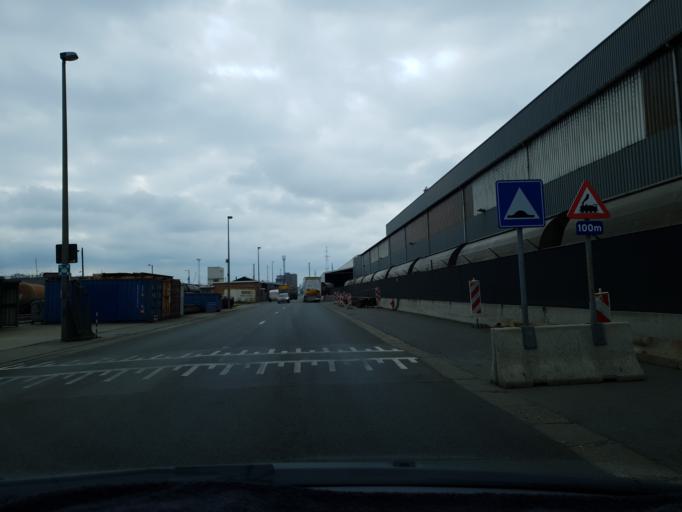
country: BE
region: Flanders
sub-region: Provincie Antwerpen
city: Antwerpen
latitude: 51.2579
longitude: 4.3758
